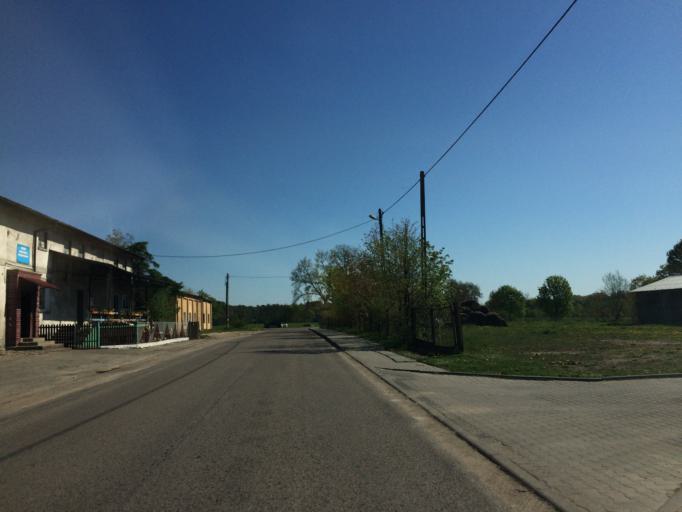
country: PL
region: Warmian-Masurian Voivodeship
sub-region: Powiat ostrodzki
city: Dabrowno
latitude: 53.4972
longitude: 19.9767
